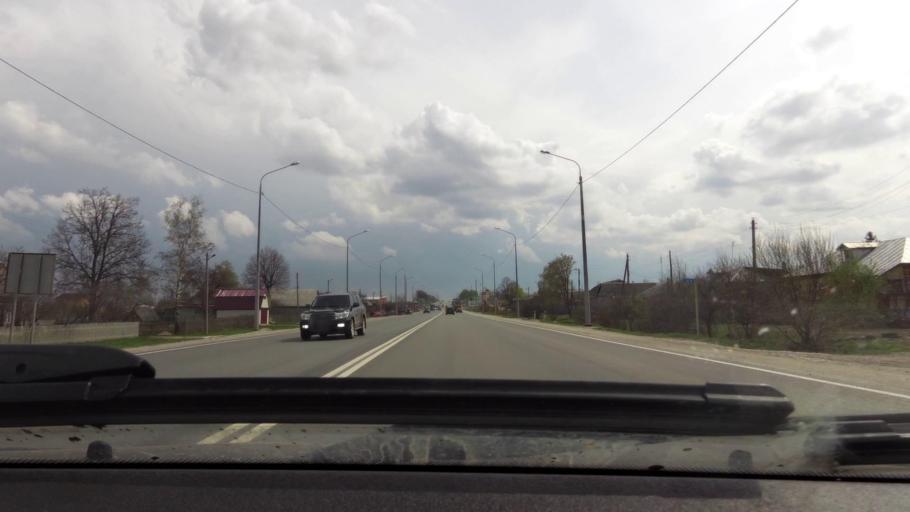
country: RU
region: Rjazan
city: Bagramovo
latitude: 54.7313
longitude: 39.4619
